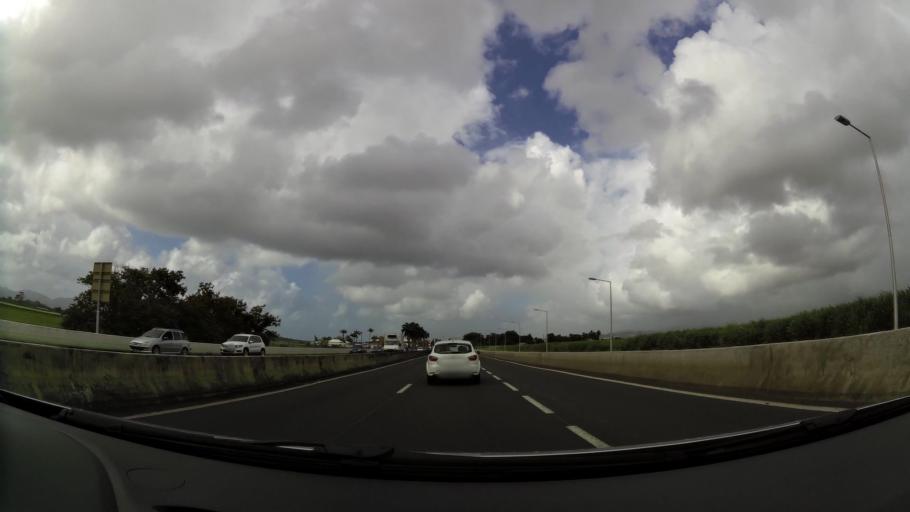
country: MQ
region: Martinique
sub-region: Martinique
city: Ducos
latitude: 14.5959
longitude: -60.9869
